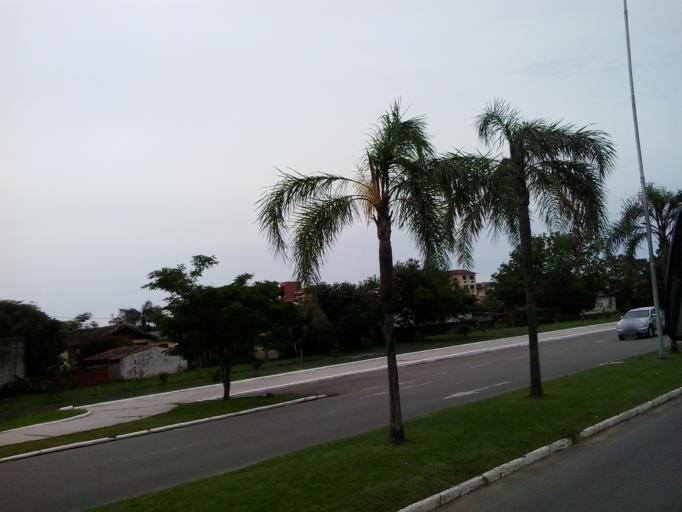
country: BR
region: Rio Grande do Sul
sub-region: Santa Maria
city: Santa Maria
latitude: -29.7035
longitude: -53.7157
